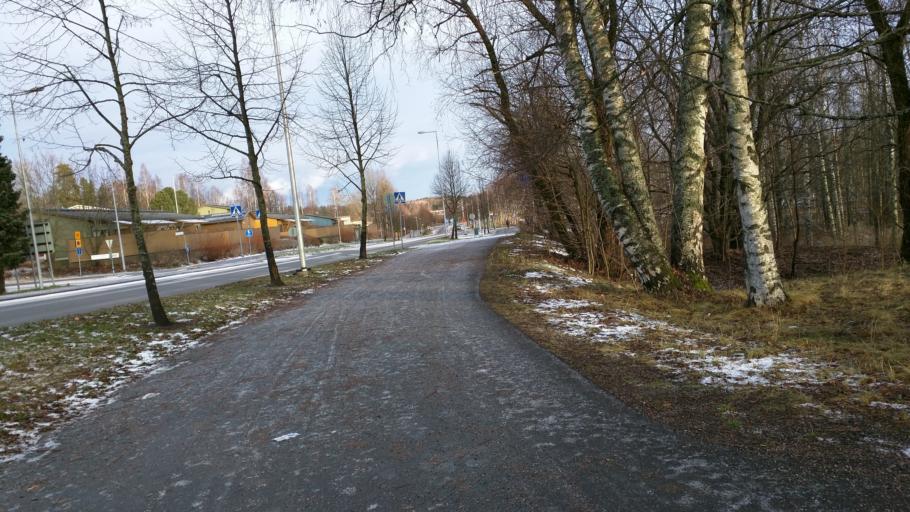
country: FI
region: Uusimaa
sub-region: Helsinki
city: Kilo
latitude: 60.2641
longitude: 24.8114
